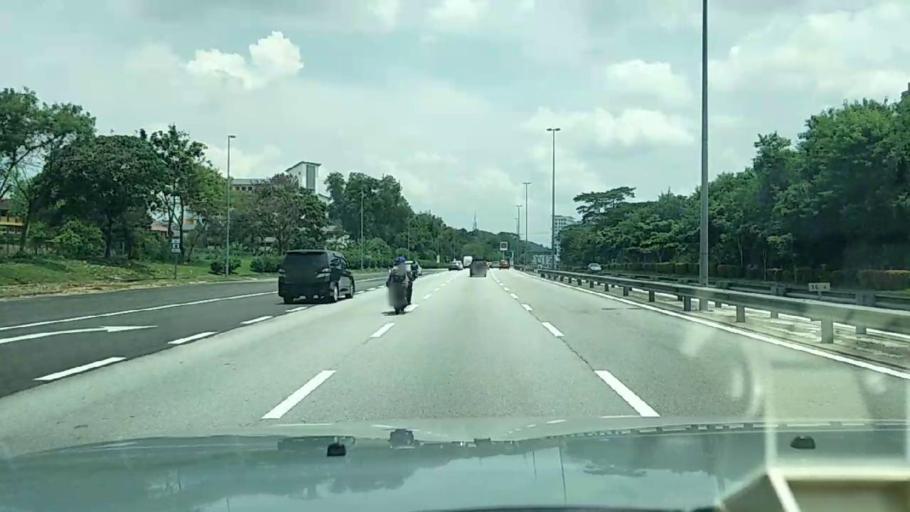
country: MY
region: Kuala Lumpur
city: Kuala Lumpur
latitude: 3.0941
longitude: 101.6858
